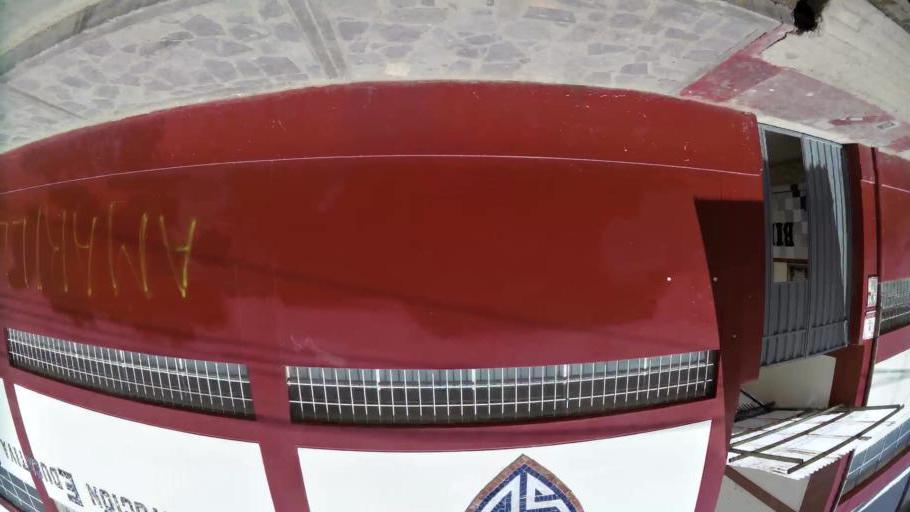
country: PE
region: Junin
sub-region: Provincia de Jauja
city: Jauja
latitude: -11.7756
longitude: -75.4963
